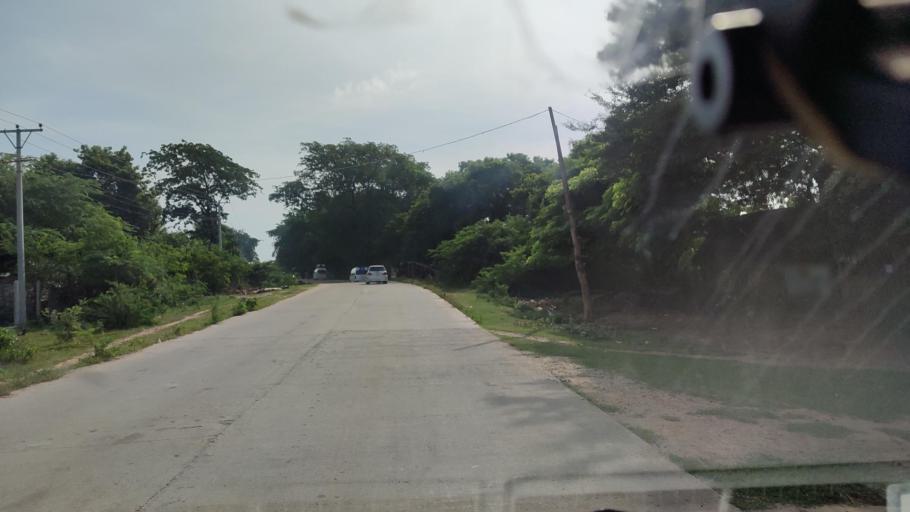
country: MM
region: Magway
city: Pakokku
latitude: 21.3303
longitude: 95.2531
